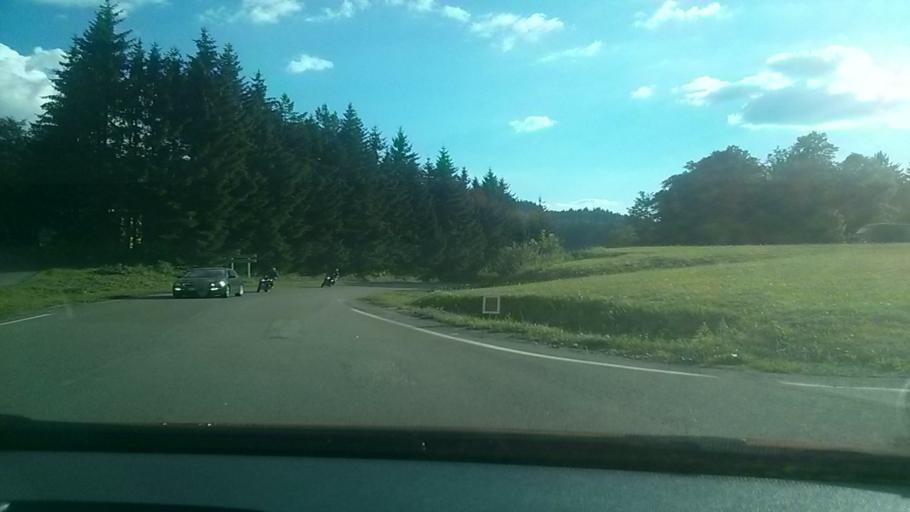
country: FR
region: Franche-Comte
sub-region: Departement du Jura
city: Les Rousses
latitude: 46.4617
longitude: 6.0712
